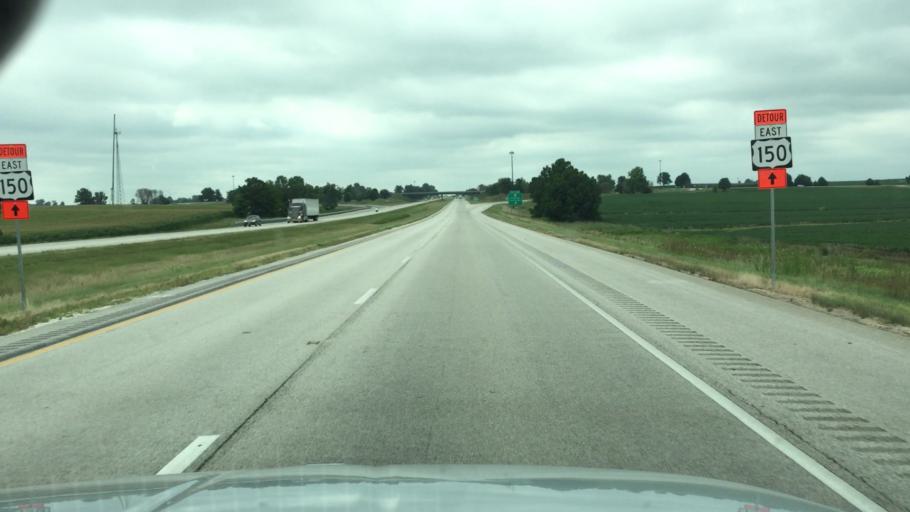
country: US
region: Illinois
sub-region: Henry County
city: Orion
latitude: 41.3024
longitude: -90.3342
